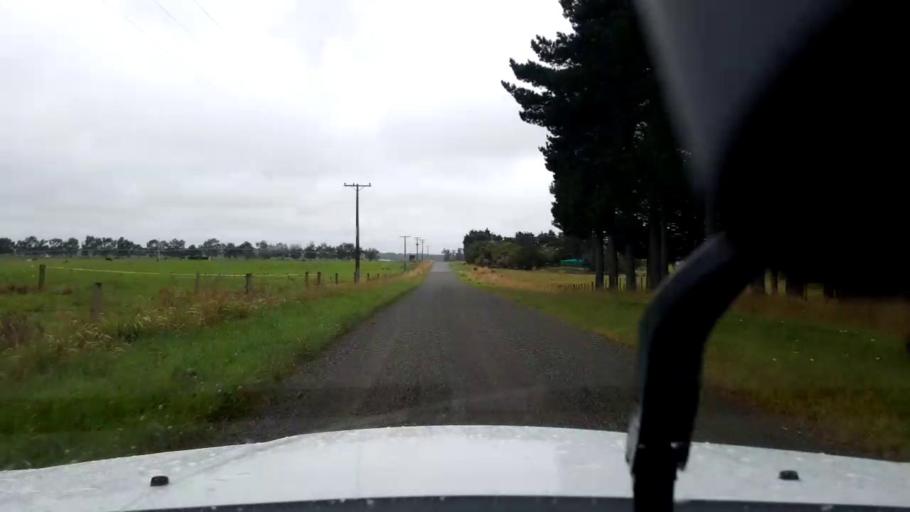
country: NZ
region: Canterbury
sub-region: Timaru District
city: Pleasant Point
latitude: -44.2420
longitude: 171.2014
